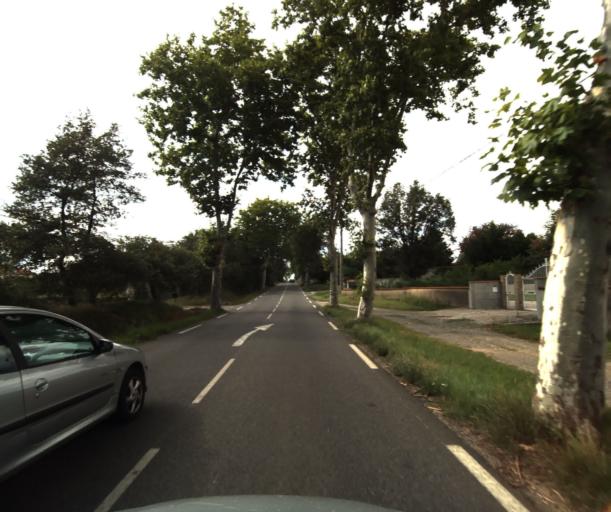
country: FR
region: Midi-Pyrenees
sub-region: Departement de la Haute-Garonne
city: Eaunes
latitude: 43.4395
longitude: 1.3412
